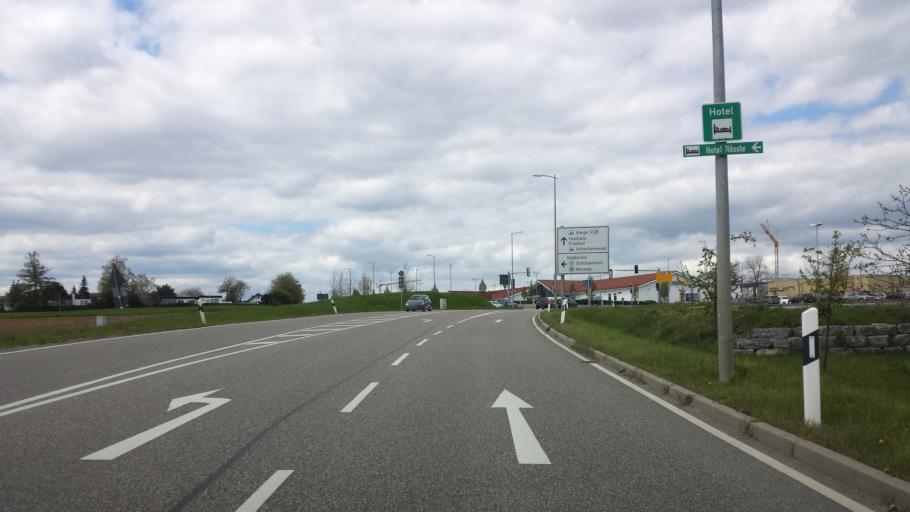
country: DE
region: Baden-Wuerttemberg
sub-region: Regierungsbezirk Stuttgart
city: Rutesheim
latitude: 48.8059
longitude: 8.9582
